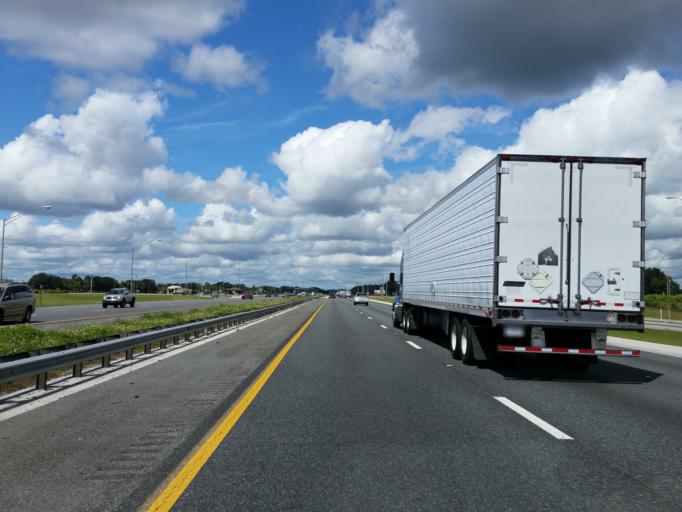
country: US
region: Florida
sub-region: Marion County
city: Belleview
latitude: 28.9889
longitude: -82.1408
